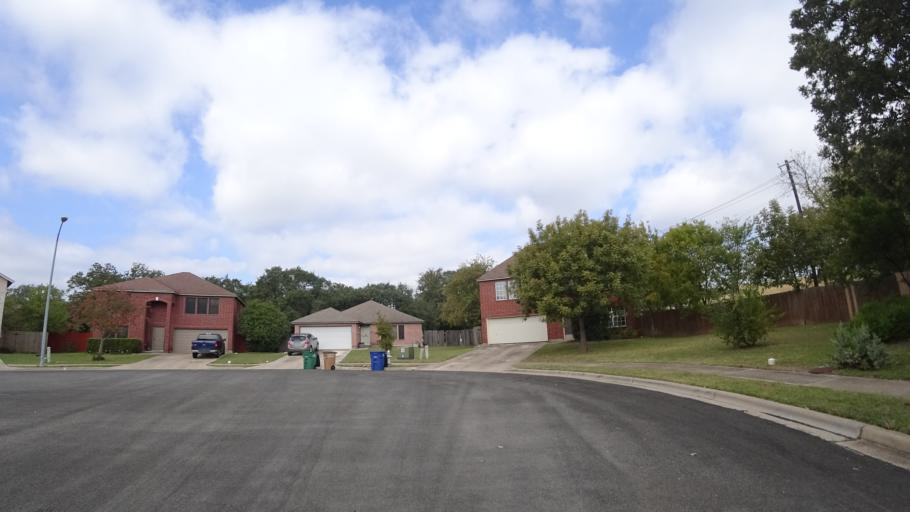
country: US
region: Texas
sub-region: Travis County
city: Shady Hollow
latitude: 30.2153
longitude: -97.8438
